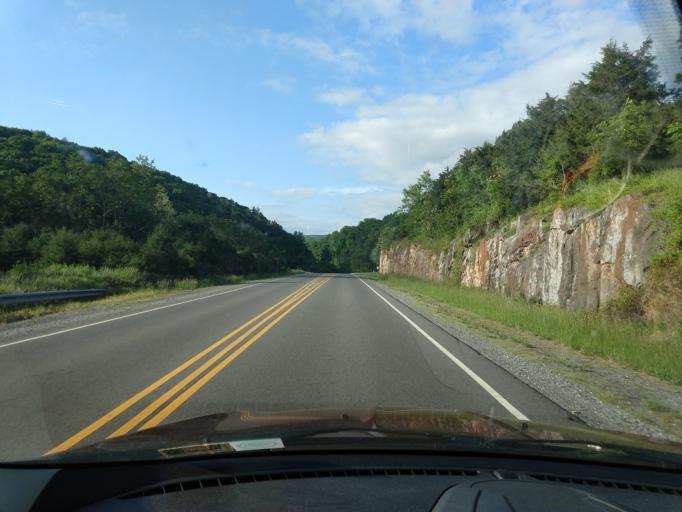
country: US
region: Virginia
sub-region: Wythe County
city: Wytheville
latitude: 36.8540
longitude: -80.9768
